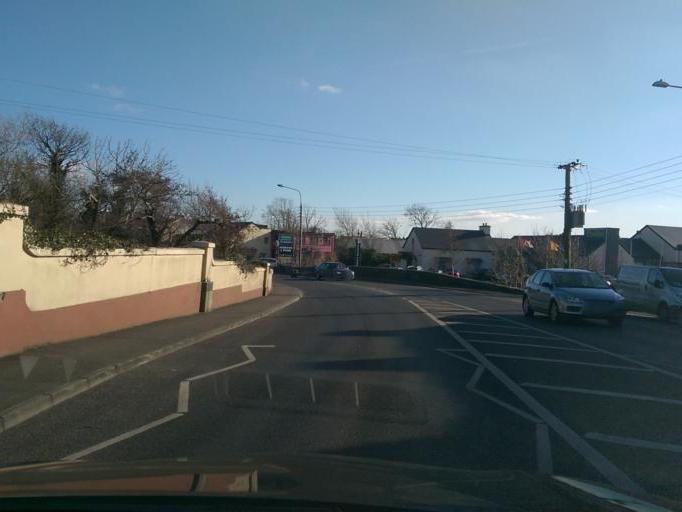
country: IE
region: Connaught
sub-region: County Galway
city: Oranmore
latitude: 53.2283
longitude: -8.8805
